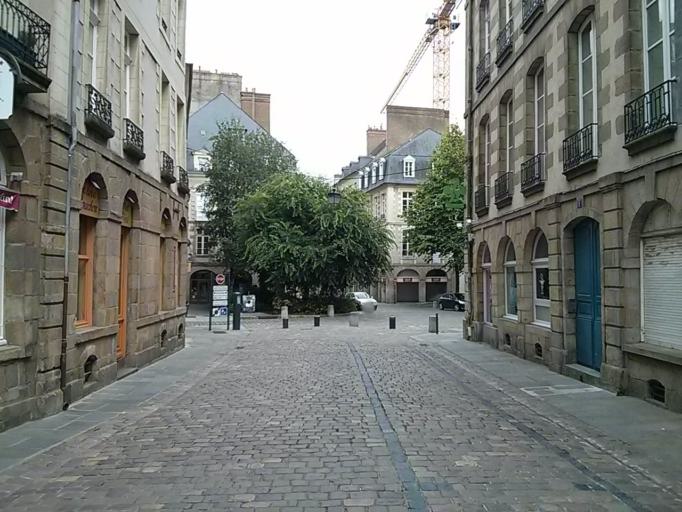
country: FR
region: Brittany
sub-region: Departement d'Ille-et-Vilaine
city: Rennes
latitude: 48.1110
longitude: -1.6818
